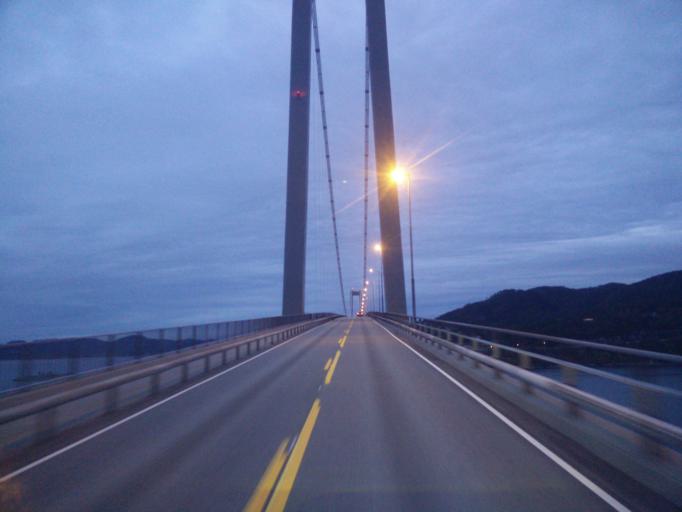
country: NO
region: More og Romsdal
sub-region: Gjemnes
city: Batnfjordsora
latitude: 62.9682
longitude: 7.7746
